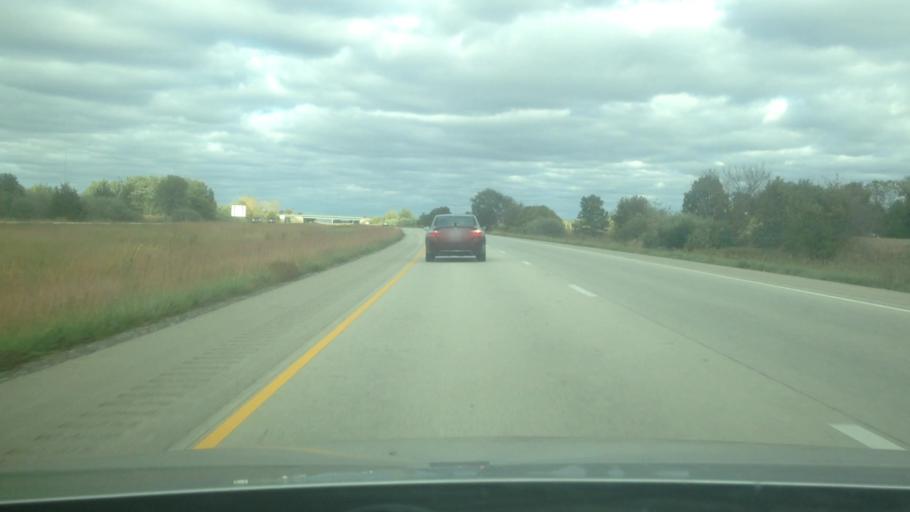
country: US
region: Illinois
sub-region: Macon County
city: Forsyth
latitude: 39.9137
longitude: -88.8683
